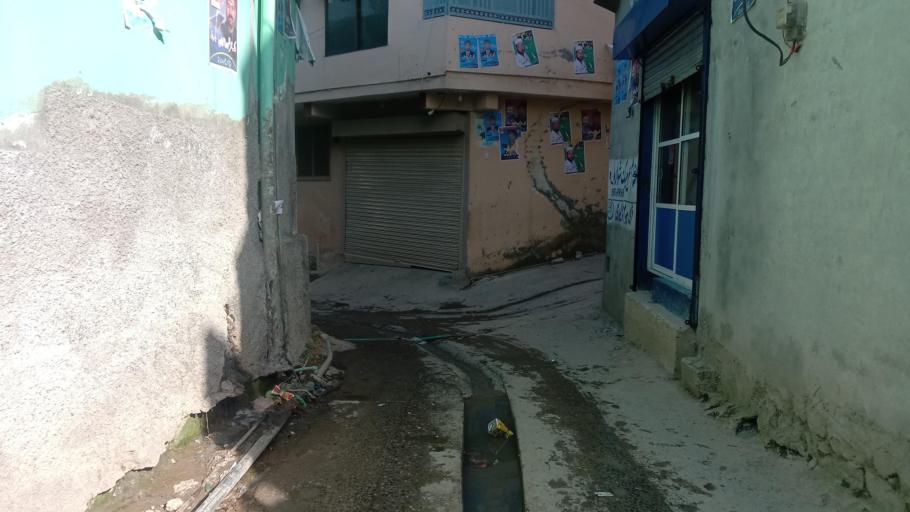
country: PK
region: Khyber Pakhtunkhwa
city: Abbottabad
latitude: 34.1813
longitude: 73.2229
